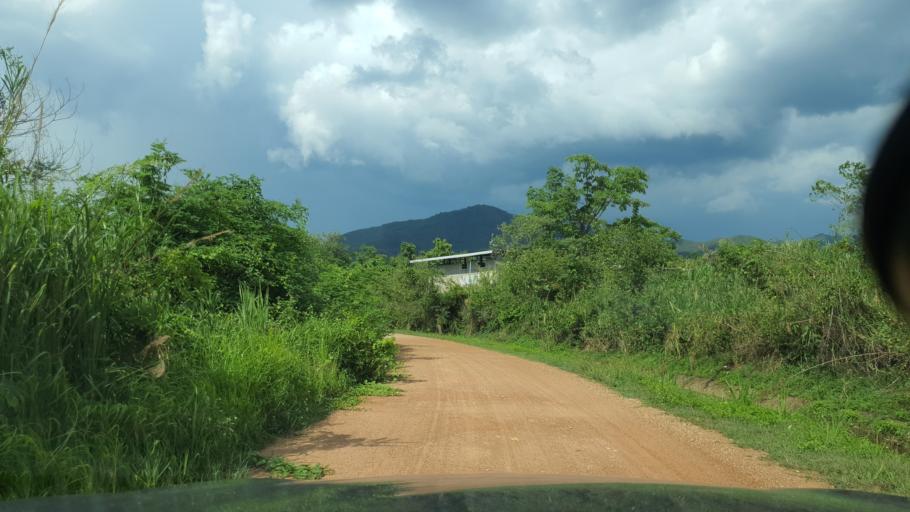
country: TH
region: Chiang Mai
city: Mae Taeng
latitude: 19.1296
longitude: 99.0465
